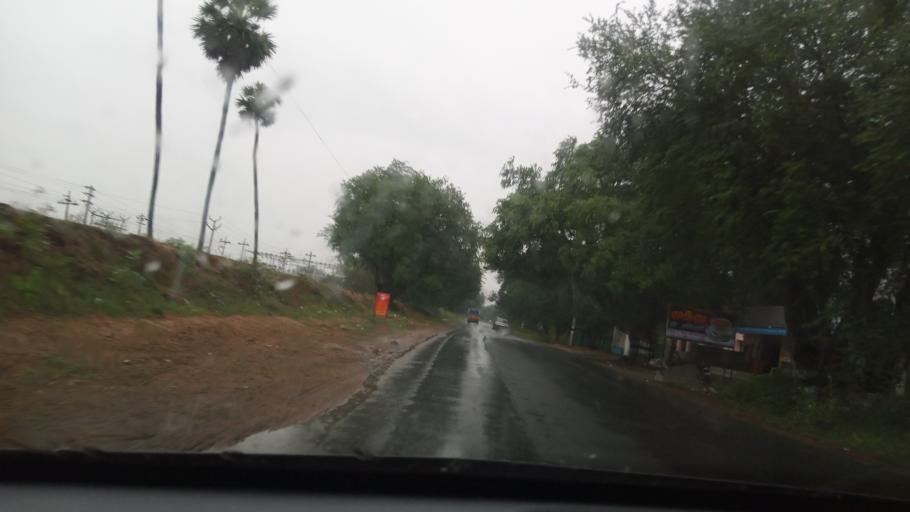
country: IN
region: Tamil Nadu
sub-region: Vellore
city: Walajapet
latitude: 12.8596
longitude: 79.3782
